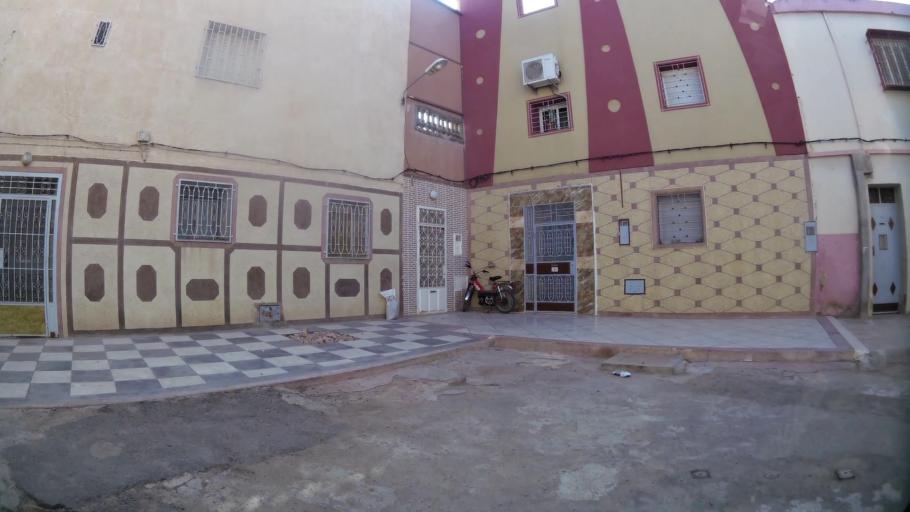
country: MA
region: Oriental
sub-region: Oujda-Angad
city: Oujda
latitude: 34.6925
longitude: -1.9051
